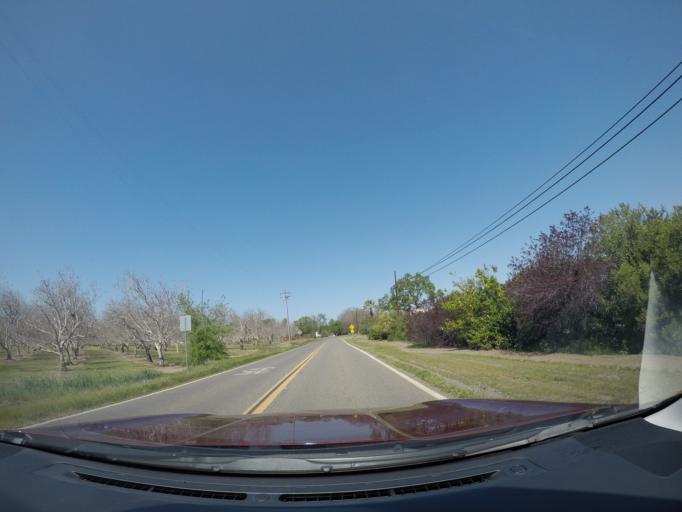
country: US
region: California
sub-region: Yolo County
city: Winters
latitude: 38.5146
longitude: -121.9676
